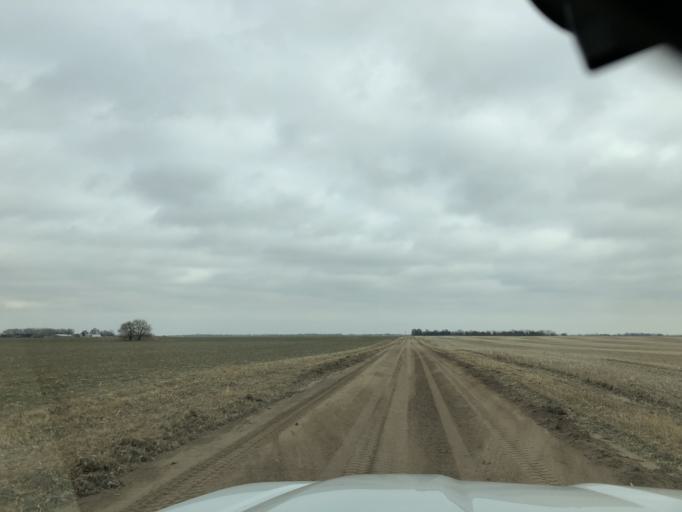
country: US
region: Kansas
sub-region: Rice County
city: Sterling
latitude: 38.0428
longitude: -98.2292
